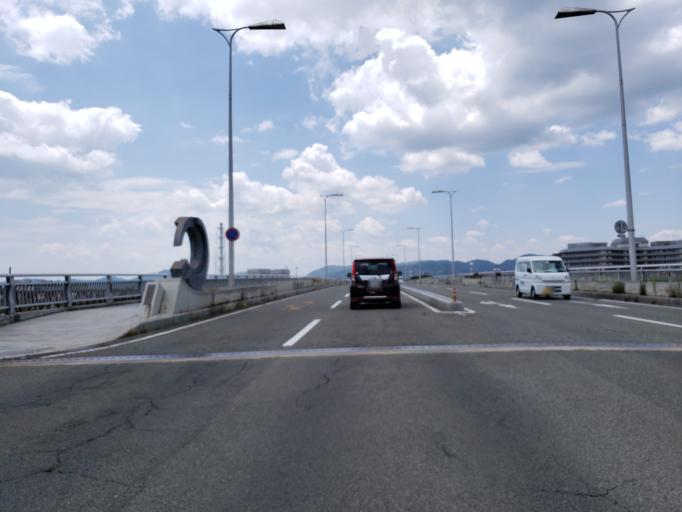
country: JP
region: Hyogo
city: Kariya
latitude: 34.7406
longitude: 134.3944
